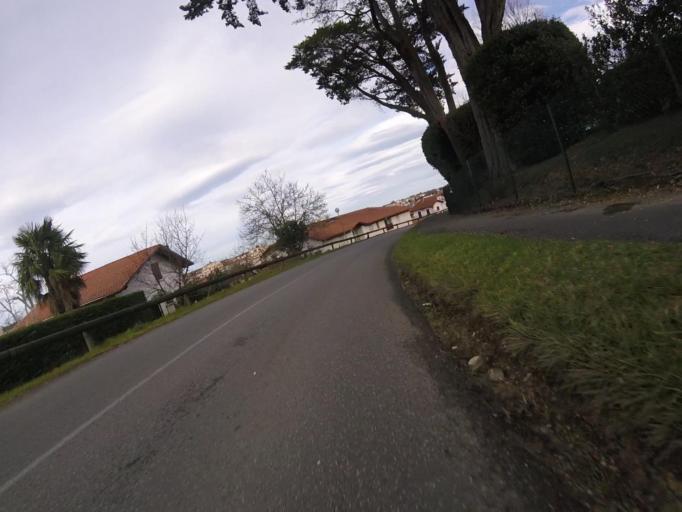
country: FR
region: Aquitaine
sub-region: Departement des Pyrenees-Atlantiques
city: Saint-Jean-de-Luz
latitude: 43.3764
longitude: -1.6608
